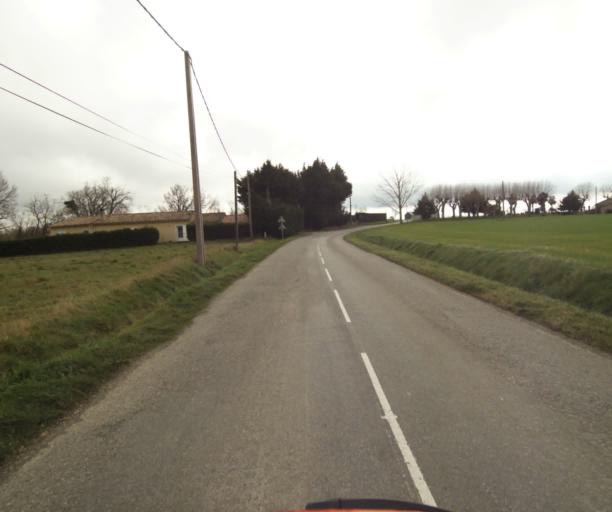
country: FR
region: Languedoc-Roussillon
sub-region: Departement de l'Aude
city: Belpech
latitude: 43.1999
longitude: 1.7340
